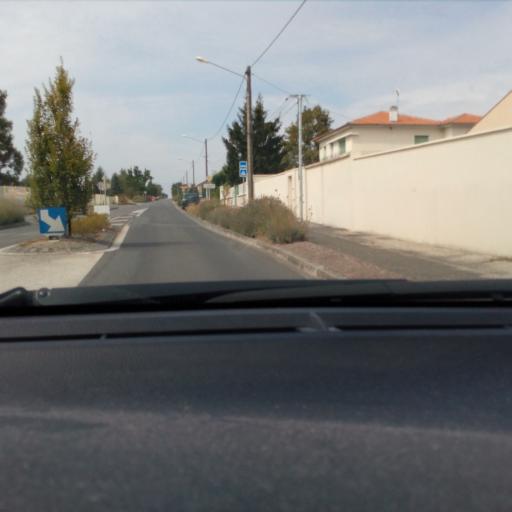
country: FR
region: Poitou-Charentes
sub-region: Departement de la Charente
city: Saint-Yrieix-sur-Charente
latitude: 45.6791
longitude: 0.1185
